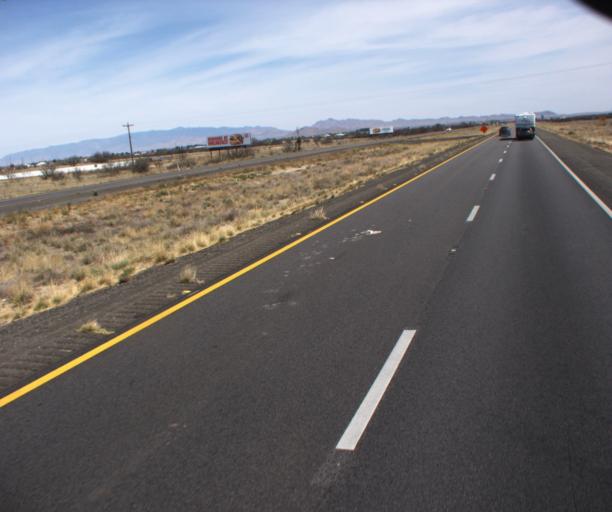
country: US
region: Arizona
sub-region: Cochise County
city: Willcox
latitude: 32.2286
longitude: -109.8731
